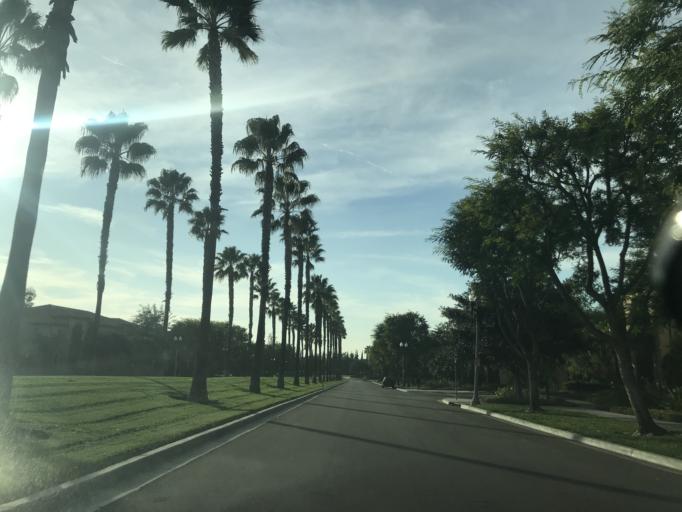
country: US
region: California
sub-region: Orange County
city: Lake Forest
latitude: 33.6977
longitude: -117.7453
